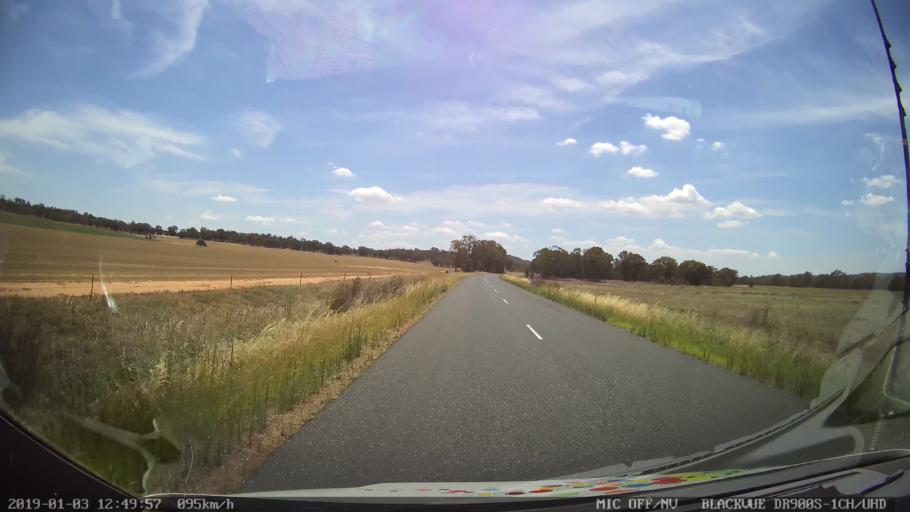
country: AU
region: New South Wales
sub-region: Weddin
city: Grenfell
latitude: -33.6970
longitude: 148.2652
